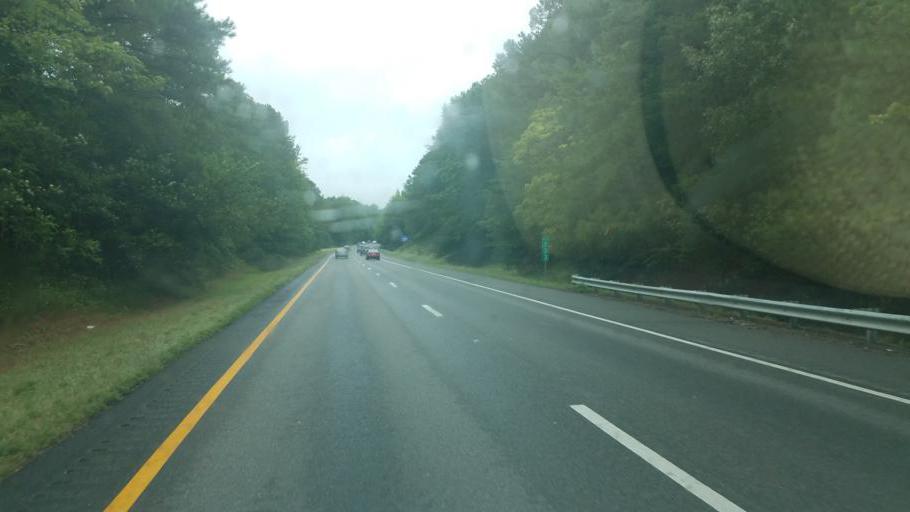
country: US
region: Virginia
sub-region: James City County
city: Williamsburg
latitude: 37.3653
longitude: -76.7454
